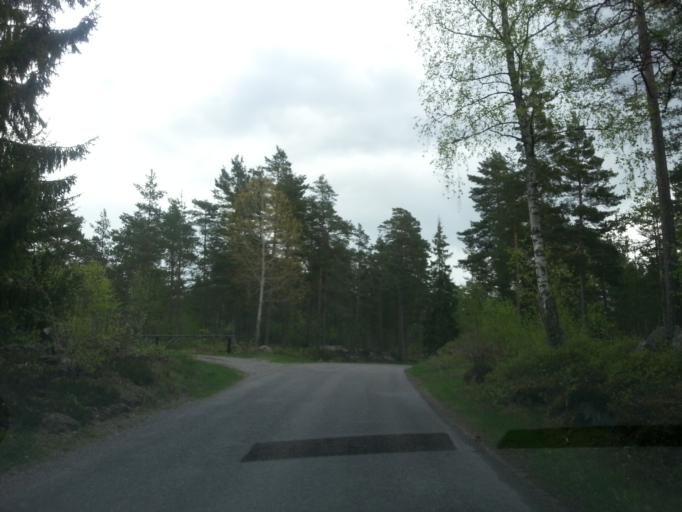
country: SE
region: OEstergoetland
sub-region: Norrkopings Kommun
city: Krokek
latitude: 58.6750
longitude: 16.3404
